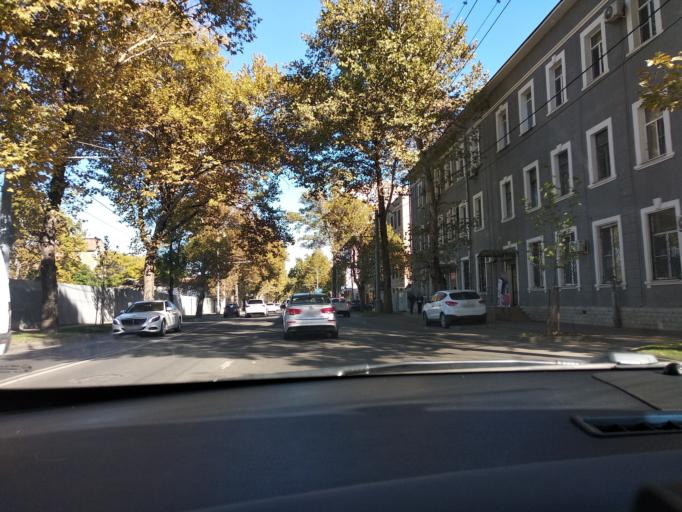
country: RU
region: Krasnodarskiy
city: Krasnodar
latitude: 45.0141
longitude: 38.9833
